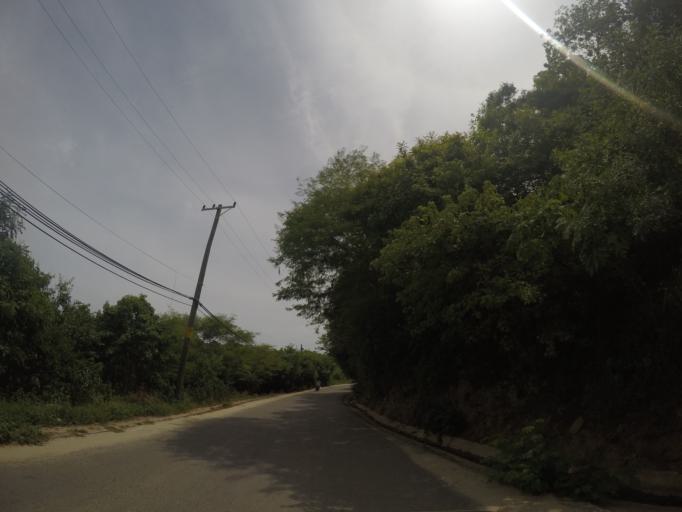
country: MX
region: Oaxaca
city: San Pedro Pochutla
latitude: 15.6653
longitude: -96.5000
